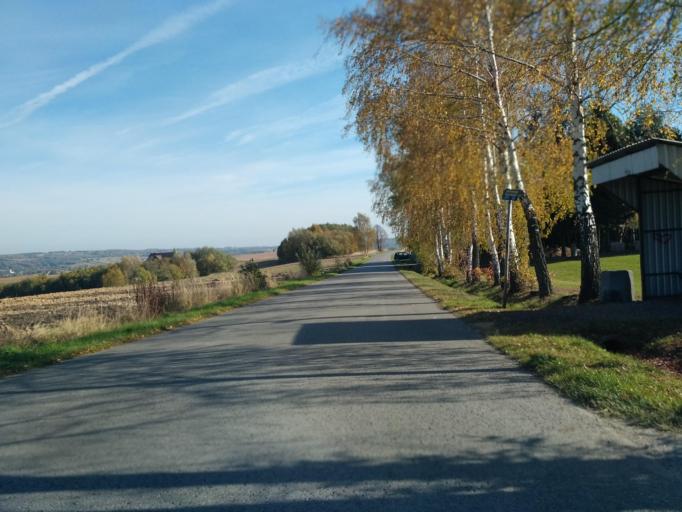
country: PL
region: Subcarpathian Voivodeship
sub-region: Powiat ropczycko-sedziszowski
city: Iwierzyce
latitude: 50.0028
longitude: 21.7396
